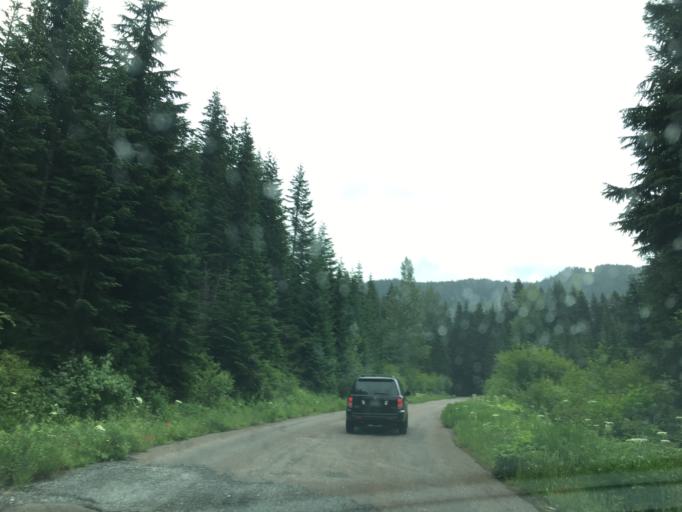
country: US
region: Washington
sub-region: Chelan County
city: Leavenworth
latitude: 47.7502
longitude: -121.1026
